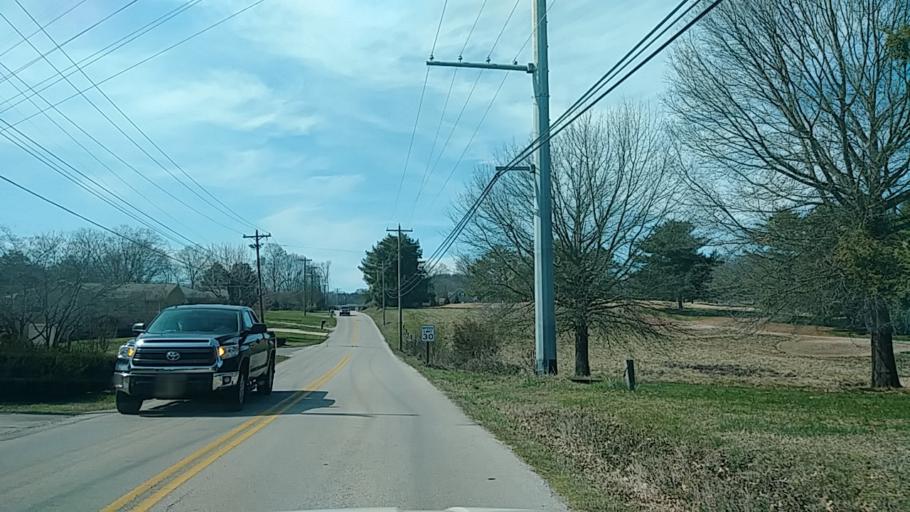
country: US
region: Tennessee
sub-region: Hamblen County
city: Morristown
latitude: 36.2122
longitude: -83.3273
